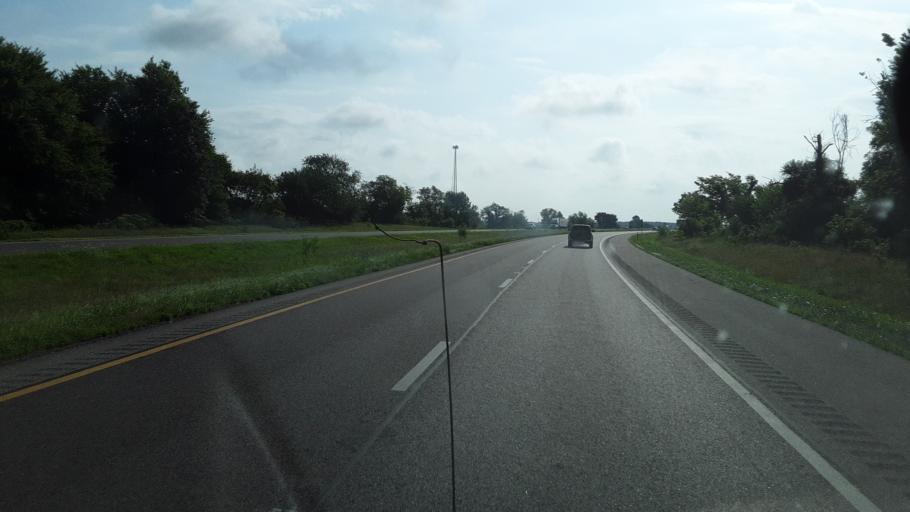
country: US
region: Illinois
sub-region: Madison County
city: Highland
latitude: 38.7836
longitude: -89.7328
